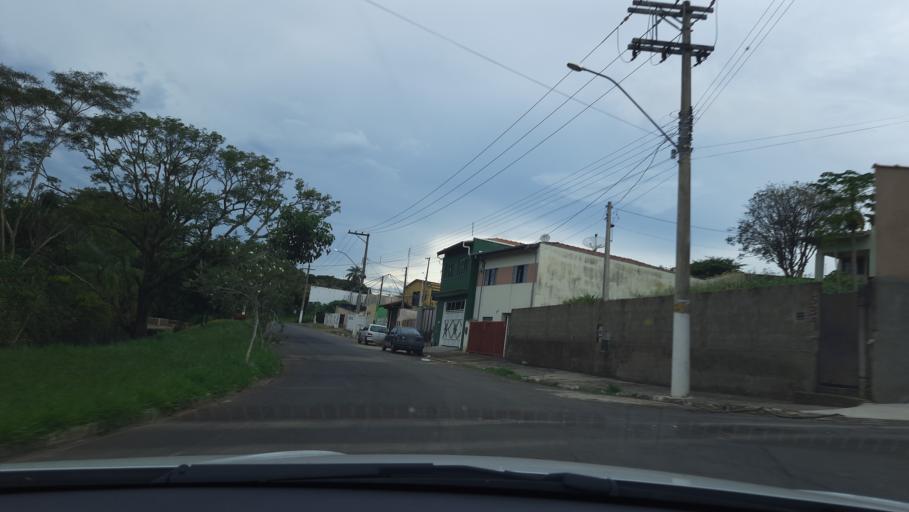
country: BR
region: Sao Paulo
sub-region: Casa Branca
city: Casa Branca
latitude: -21.7736
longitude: -47.0791
